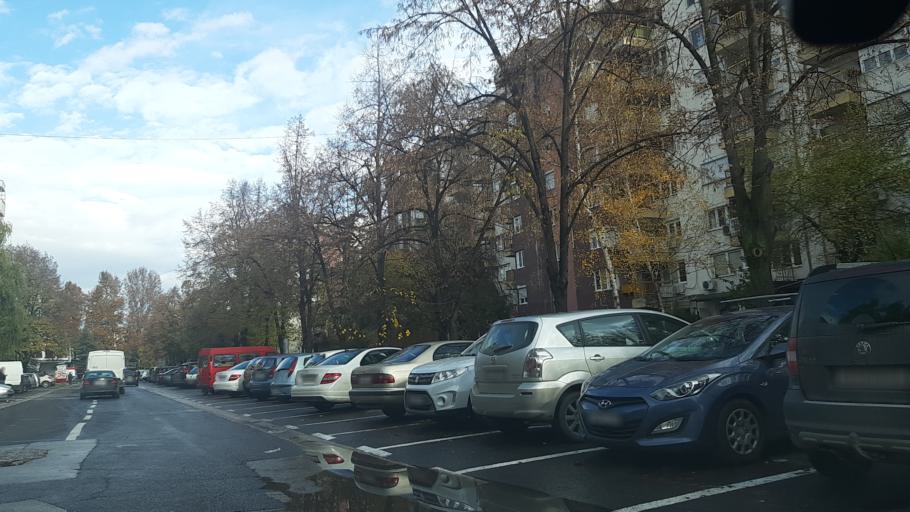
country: MK
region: Kisela Voda
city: Usje
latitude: 41.9836
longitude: 21.4650
